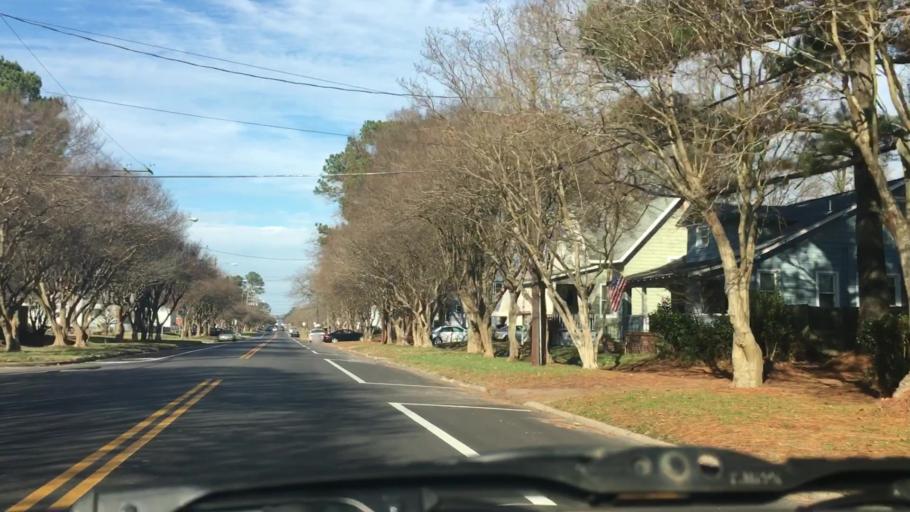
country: US
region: Virginia
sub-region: City of Norfolk
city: Norfolk
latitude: 36.8625
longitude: -76.2503
